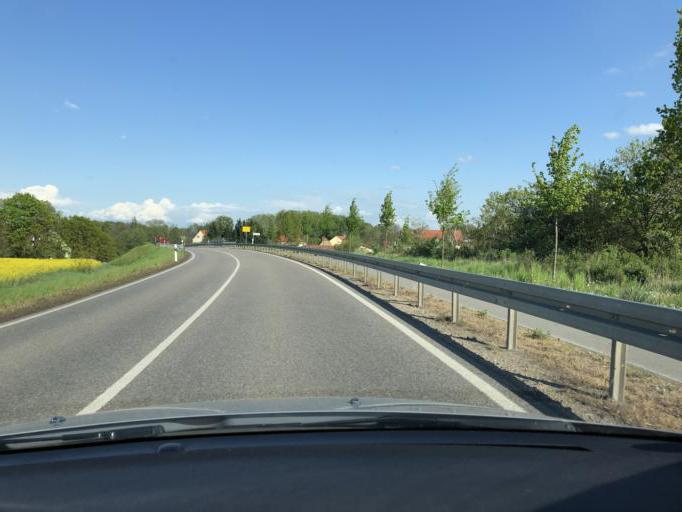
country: DE
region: Thuringia
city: Gerstenberg
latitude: 51.0327
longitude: 12.4341
